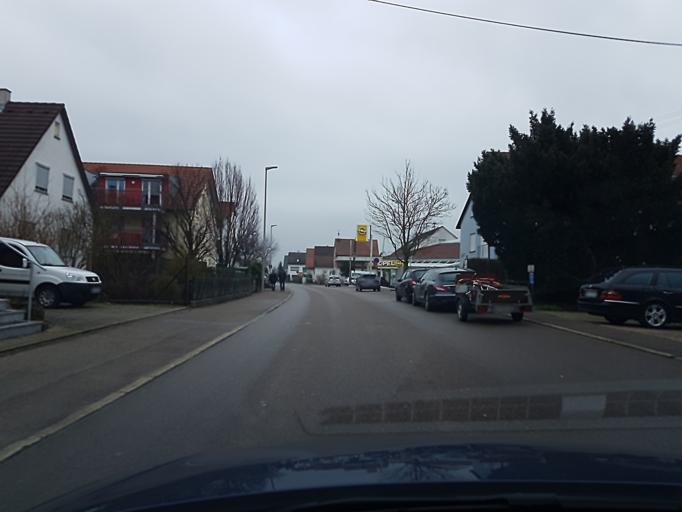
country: DE
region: Baden-Wuerttemberg
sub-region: Regierungsbezirk Stuttgart
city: Freiberg am Neckar
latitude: 48.9357
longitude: 9.1871
